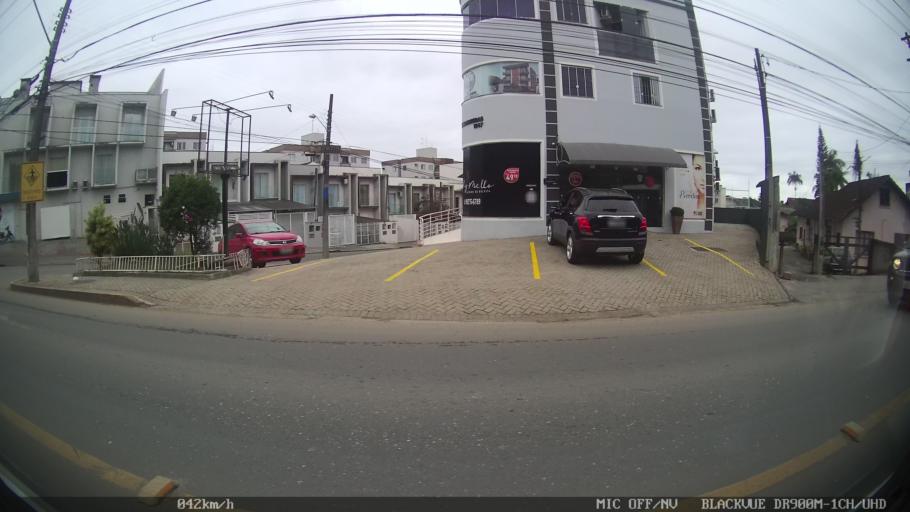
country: BR
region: Santa Catarina
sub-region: Joinville
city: Joinville
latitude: -26.2658
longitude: -48.8764
